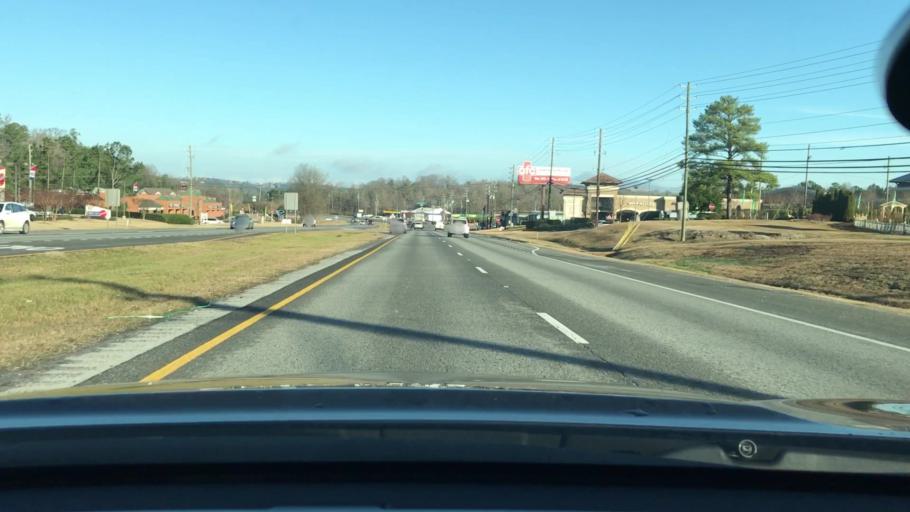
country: US
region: Alabama
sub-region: Shelby County
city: Lake Purdy
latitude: 33.4098
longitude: -86.6644
